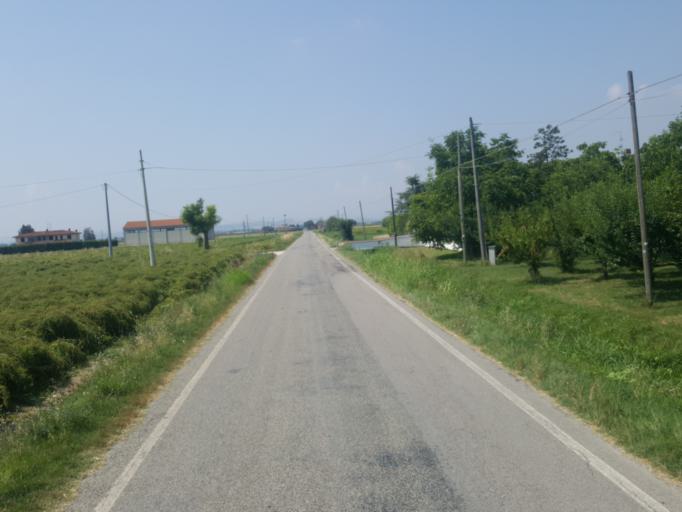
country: IT
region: Emilia-Romagna
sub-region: Provincia di Bologna
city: Sesto Imolese
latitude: 44.4559
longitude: 11.7000
